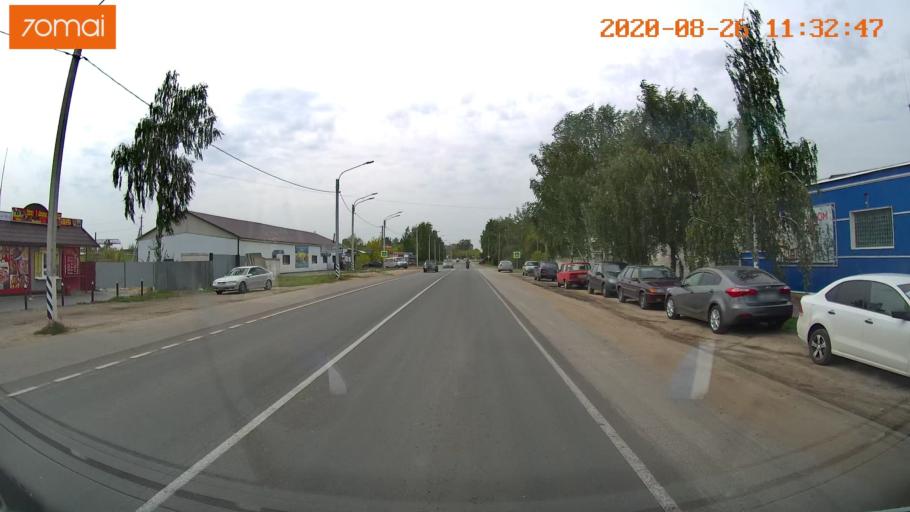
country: RU
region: Rjazan
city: Shilovo
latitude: 54.3001
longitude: 40.8614
